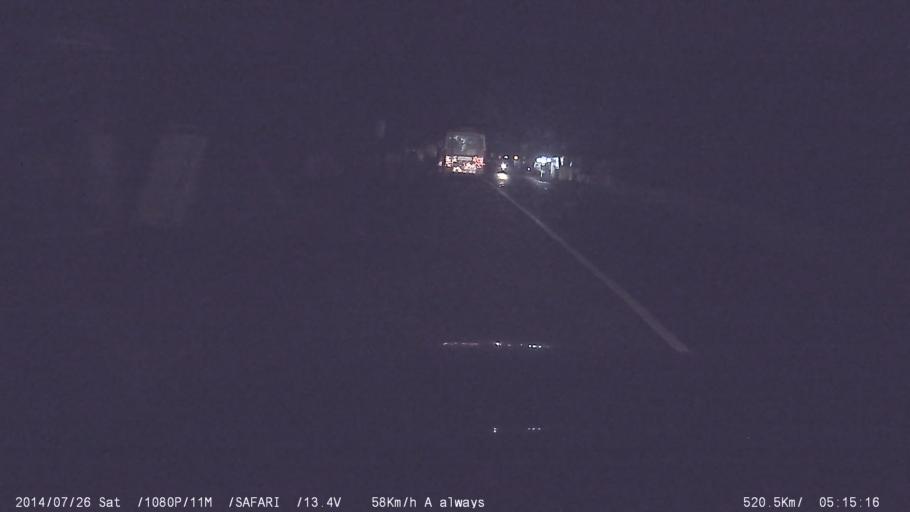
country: IN
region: Kerala
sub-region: Ernakulam
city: Muvattupula
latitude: 10.0267
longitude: 76.5539
